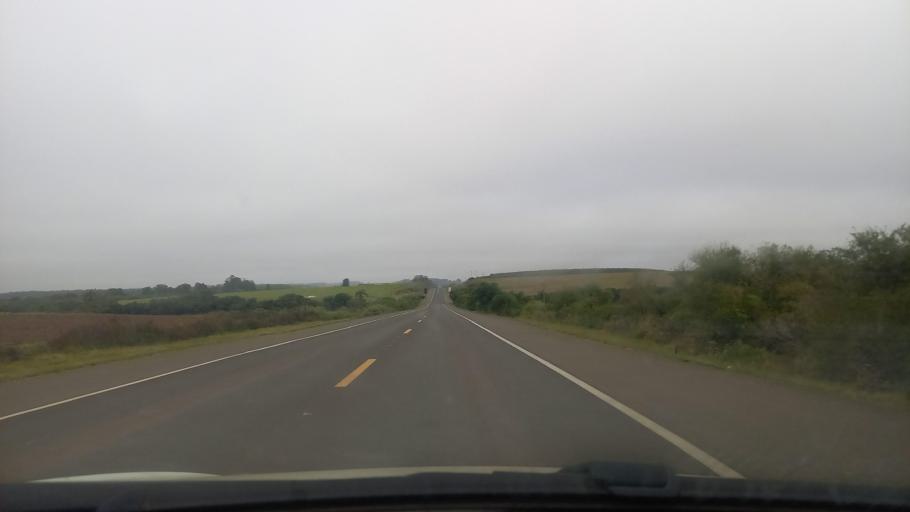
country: BR
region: Rio Grande do Sul
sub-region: Rosario Do Sul
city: Rosario do Sul
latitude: -30.2825
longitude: -54.9820
